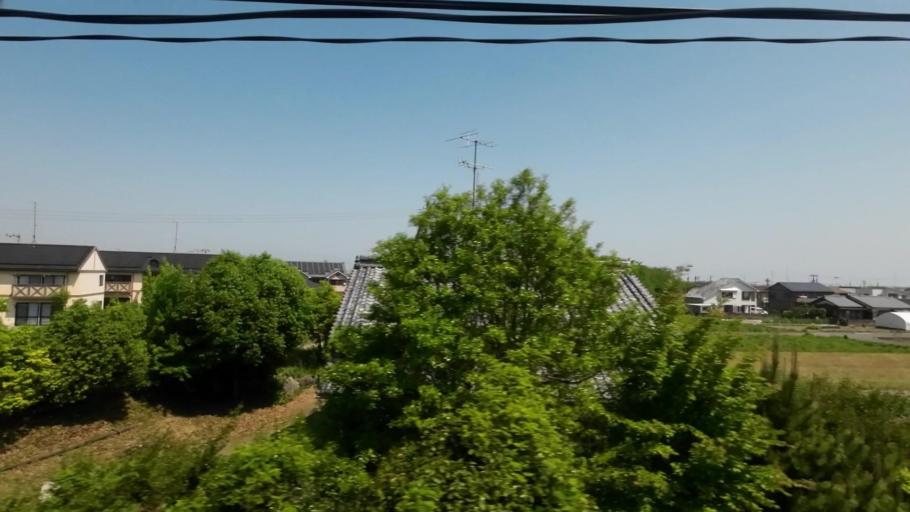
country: JP
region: Ehime
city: Saijo
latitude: 33.8980
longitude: 133.1102
